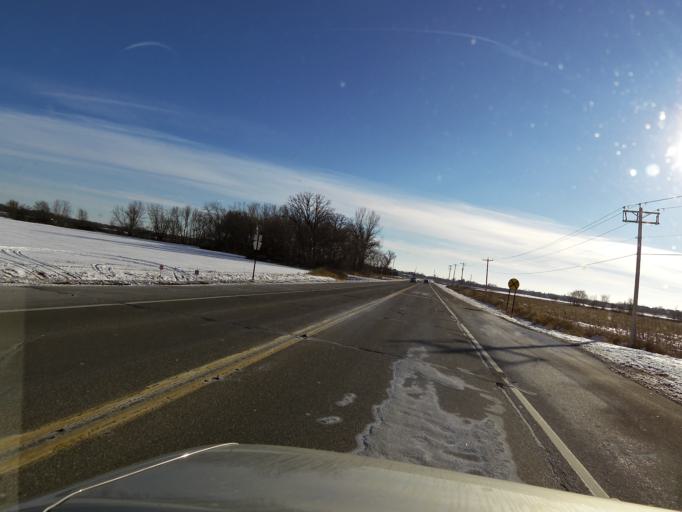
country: US
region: Minnesota
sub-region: Washington County
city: Lake Elmo
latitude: 45.0051
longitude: -92.8628
